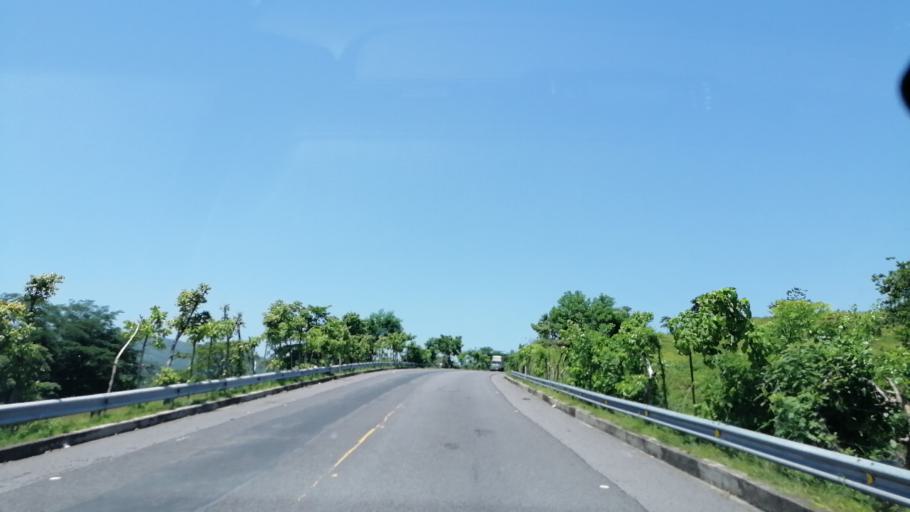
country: SV
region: Chalatenango
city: Chalatenango
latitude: 14.0300
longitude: -88.9440
